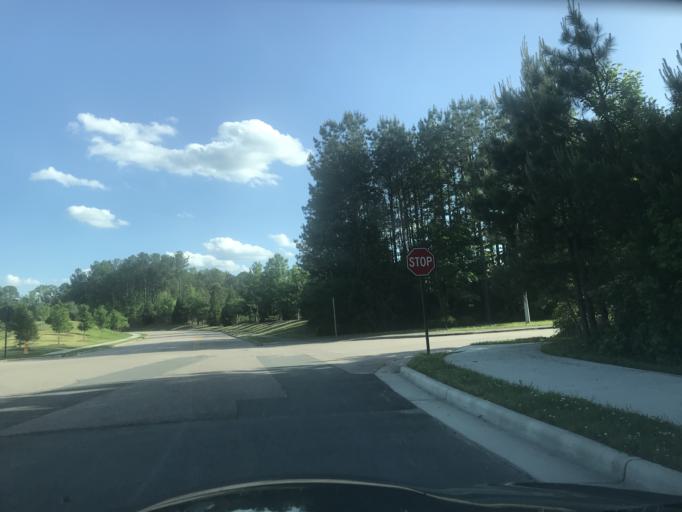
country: US
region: North Carolina
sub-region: Wake County
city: Knightdale
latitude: 35.7624
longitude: -78.4286
